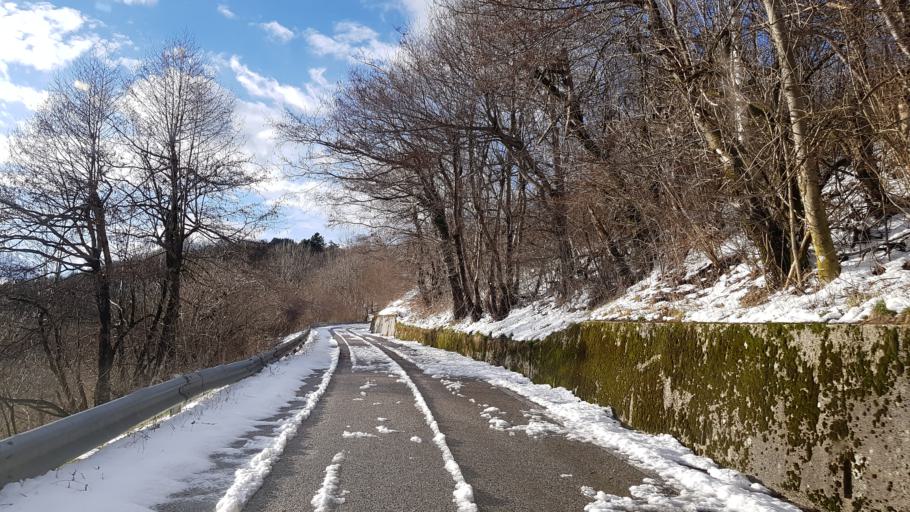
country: IT
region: Friuli Venezia Giulia
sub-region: Provincia di Udine
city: Faedis
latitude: 46.1821
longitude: 13.3919
